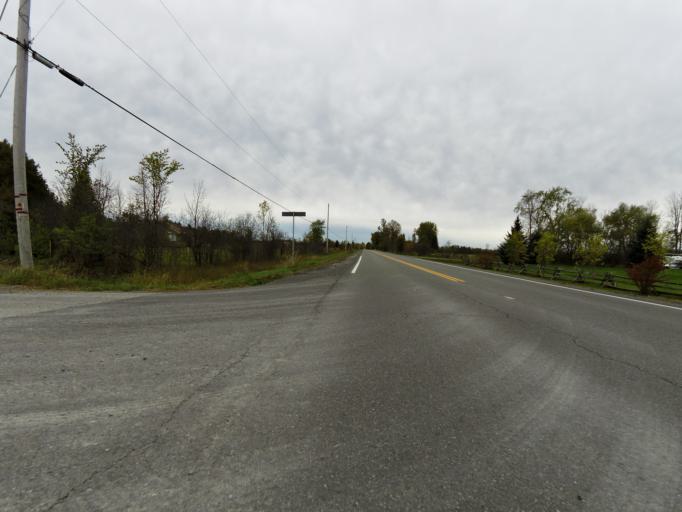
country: CA
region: Ontario
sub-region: Lanark County
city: Smiths Falls
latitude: 44.8636
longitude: -75.8082
